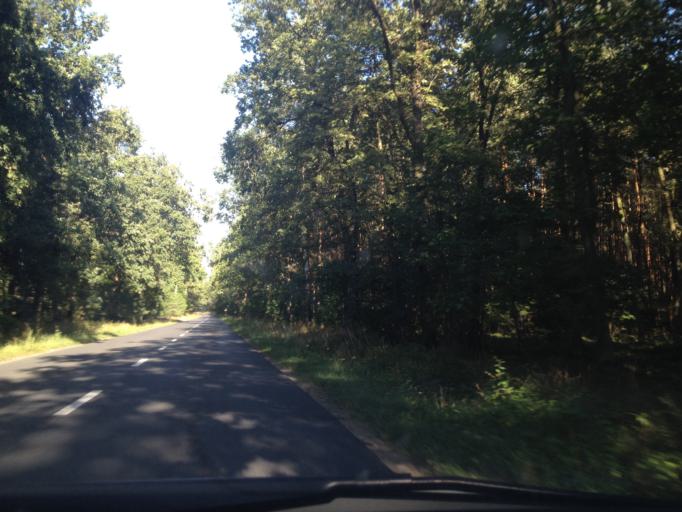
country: PL
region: Greater Poland Voivodeship
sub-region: Powiat sremski
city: Srem
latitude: 52.1058
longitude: 17.0549
